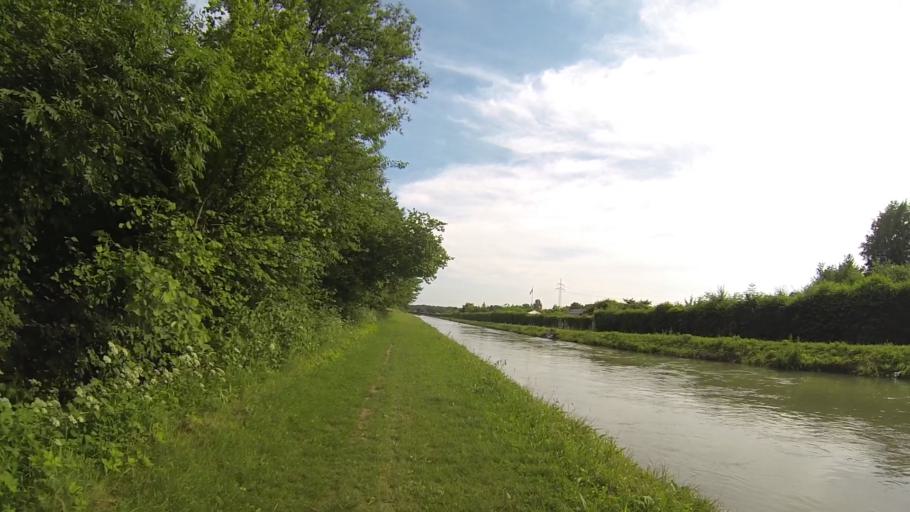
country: DE
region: Baden-Wuerttemberg
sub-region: Tuebingen Region
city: Ulm
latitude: 48.3797
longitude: 9.9950
